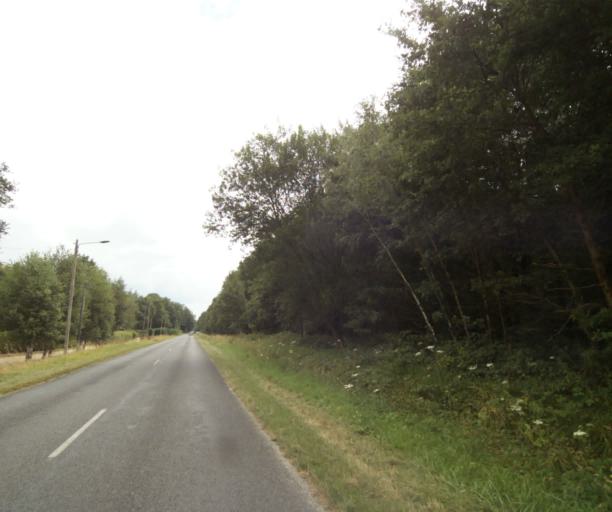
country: FR
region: Centre
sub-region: Departement du Loiret
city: Mardie
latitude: 47.8995
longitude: 2.0766
